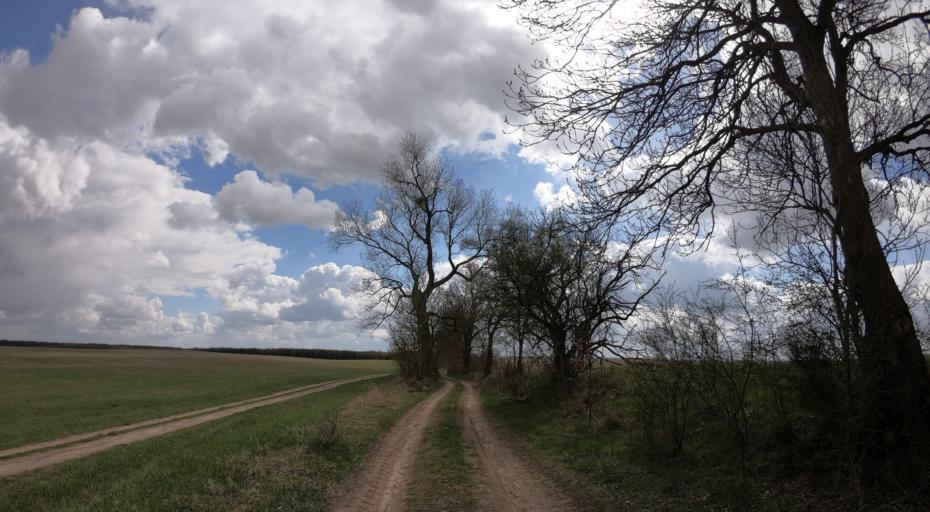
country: PL
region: West Pomeranian Voivodeship
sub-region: Powiat drawski
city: Drawsko Pomorskie
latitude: 53.5588
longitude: 15.8556
